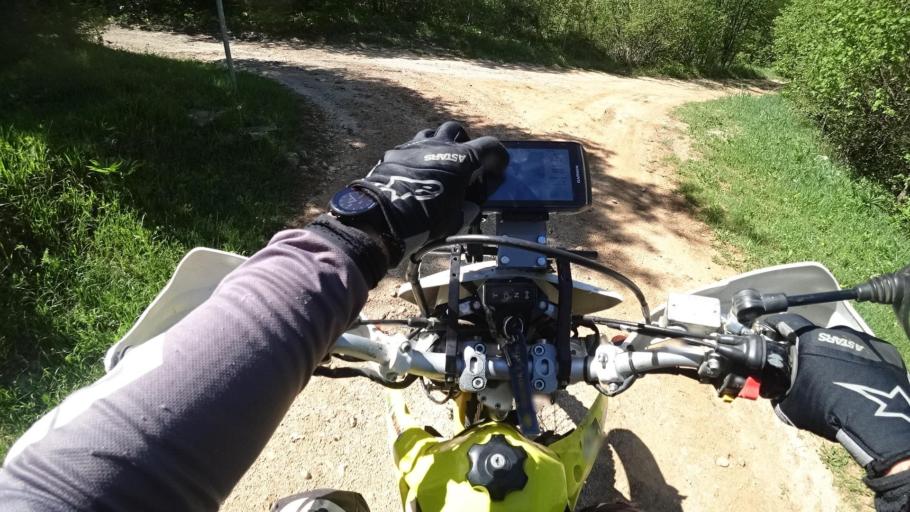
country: BA
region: Federation of Bosnia and Herzegovina
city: Gracanica
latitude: 43.7784
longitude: 18.3304
